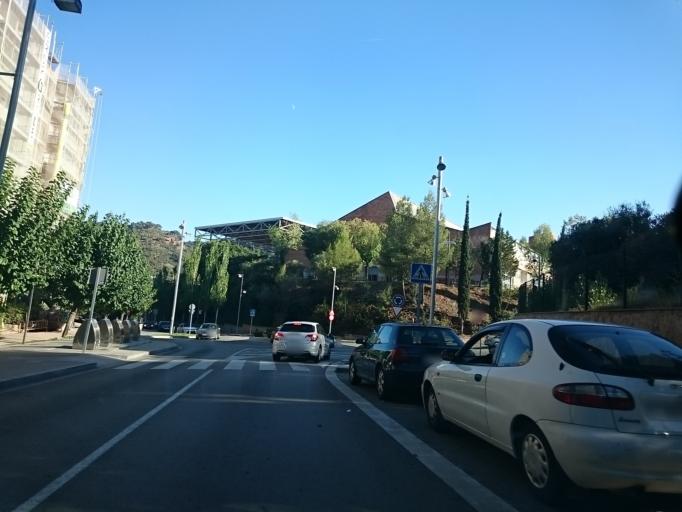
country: ES
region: Catalonia
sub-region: Provincia de Barcelona
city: Martorell
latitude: 41.4767
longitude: 1.9219
